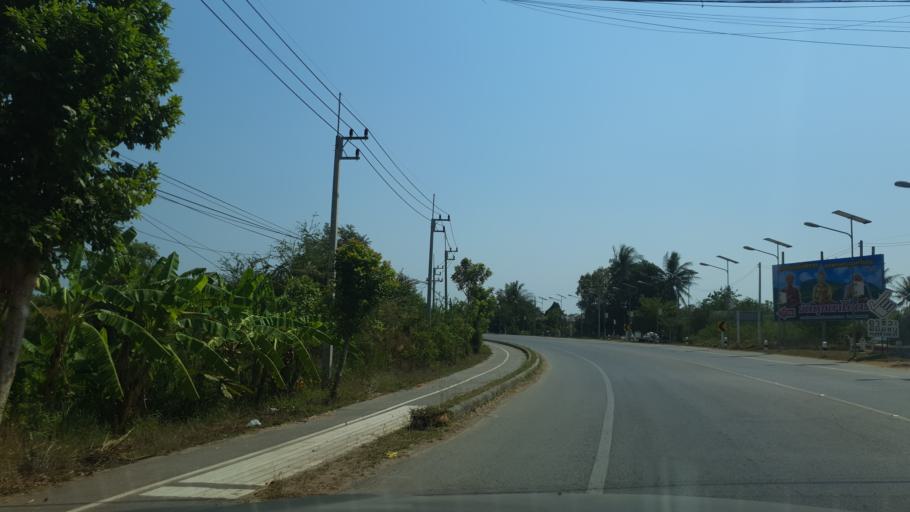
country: TH
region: Prachuap Khiri Khan
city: Pran Buri
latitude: 12.3418
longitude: 99.9437
